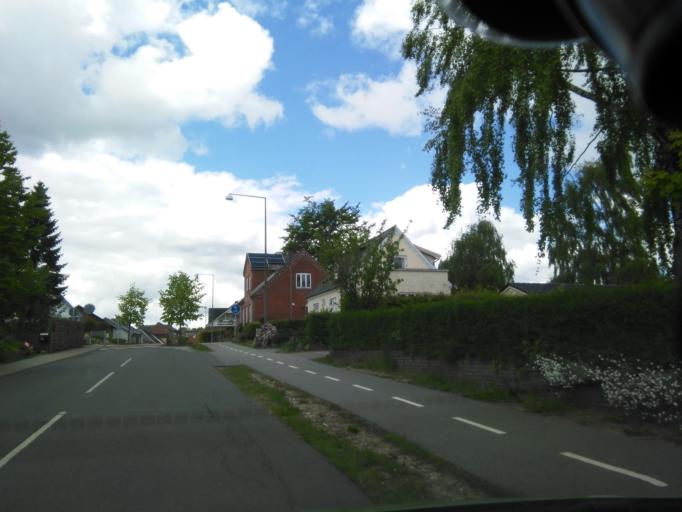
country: DK
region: Central Jutland
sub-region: Skanderborg Kommune
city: Horning
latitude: 56.0814
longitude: 10.0416
